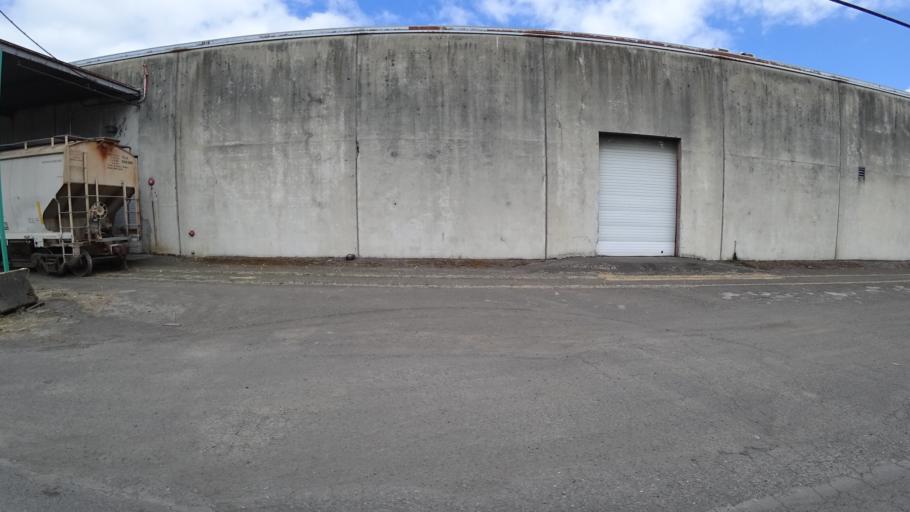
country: US
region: Oregon
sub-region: Washington County
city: Cedar Mill
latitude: 45.6130
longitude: -122.7785
